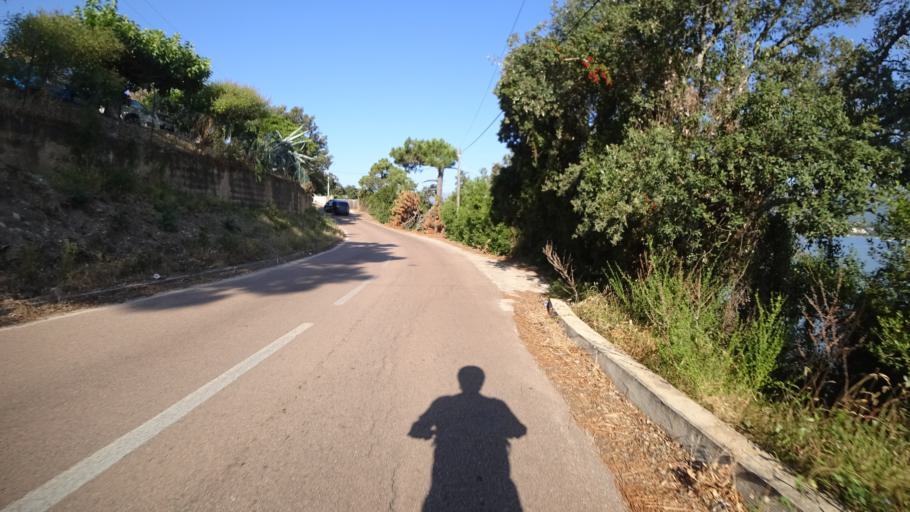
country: FR
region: Corsica
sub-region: Departement de la Corse-du-Sud
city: Porto-Vecchio
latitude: 41.6176
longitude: 9.3196
